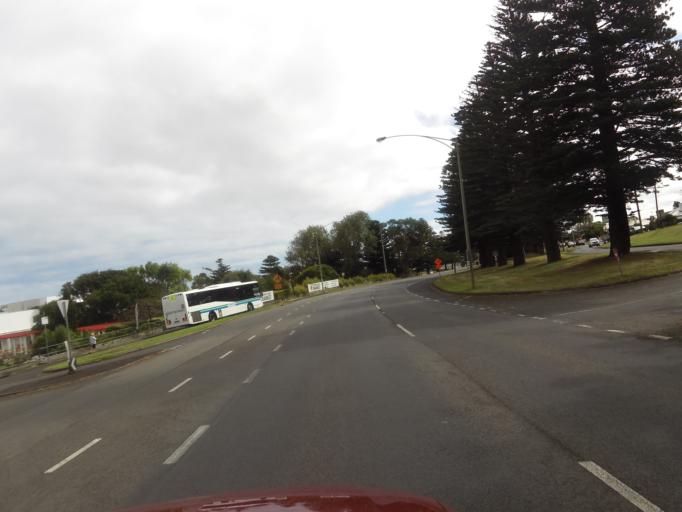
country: AU
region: Victoria
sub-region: Warrnambool
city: Warrnambool
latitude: -38.3863
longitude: 142.4985
